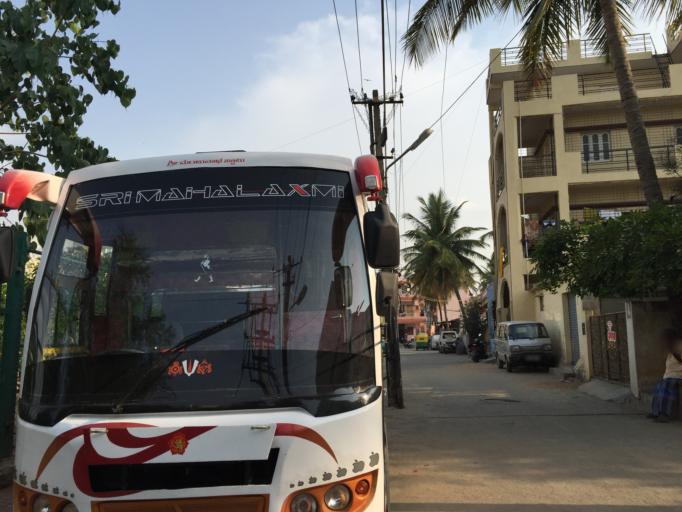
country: IN
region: Karnataka
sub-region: Bangalore Urban
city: Bangalore
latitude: 12.9439
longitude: 77.5688
